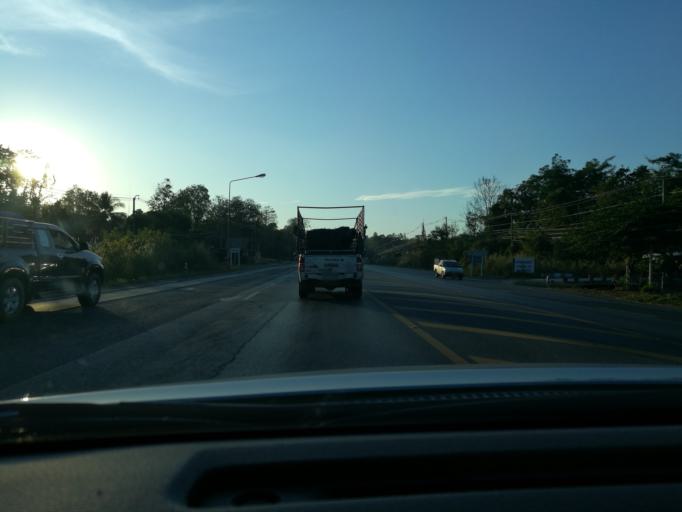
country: TH
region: Phitsanulok
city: Wang Thong
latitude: 16.8431
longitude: 100.5376
